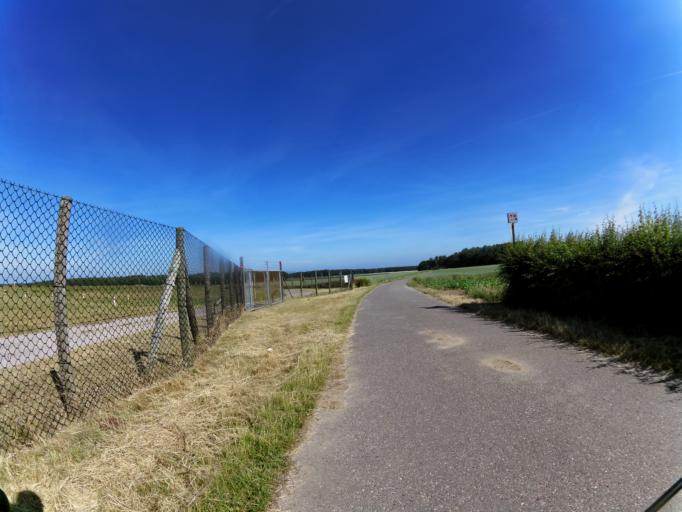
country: DE
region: North Rhine-Westphalia
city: Geilenkirchen
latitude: 50.9608
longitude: 6.0661
